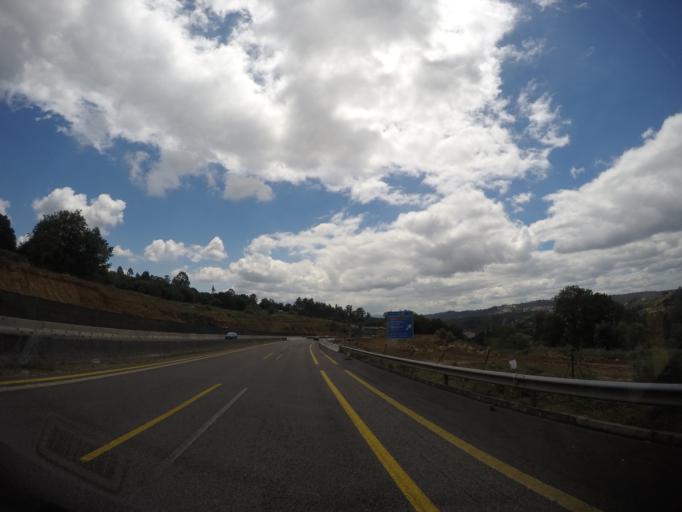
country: ES
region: Galicia
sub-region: Provincia da Coruna
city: Negreira
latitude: 42.8271
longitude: -8.7508
